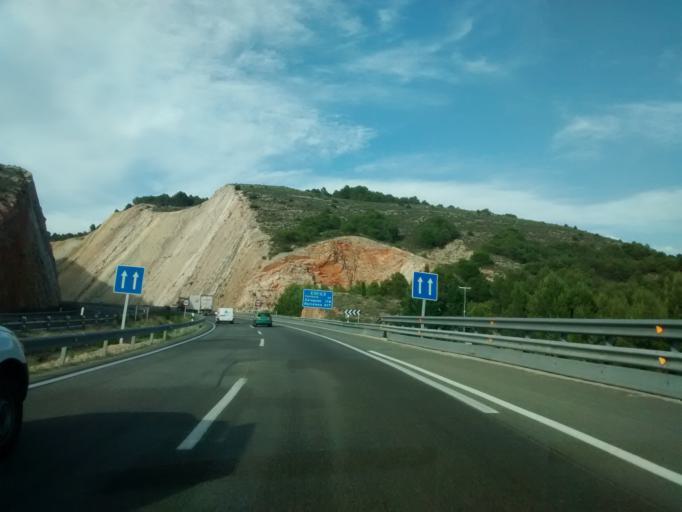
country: ES
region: Aragon
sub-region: Provincia de Zaragoza
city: Contamina
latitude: 41.3093
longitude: -1.9126
